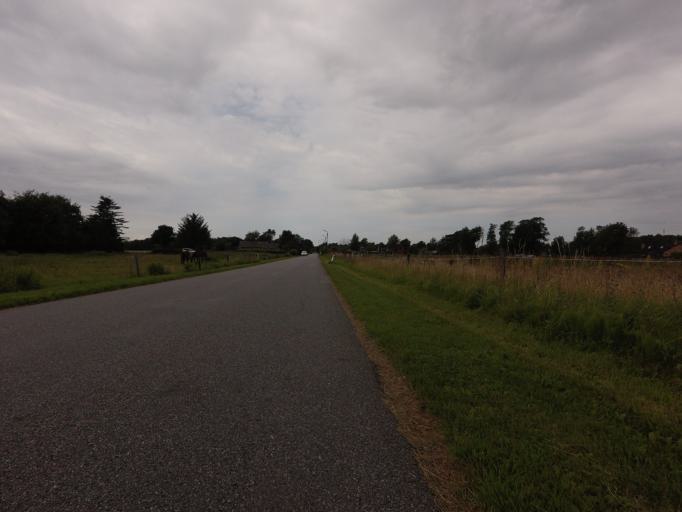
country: DK
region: North Denmark
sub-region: Alborg Kommune
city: Vadum
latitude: 57.1133
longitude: 9.8658
